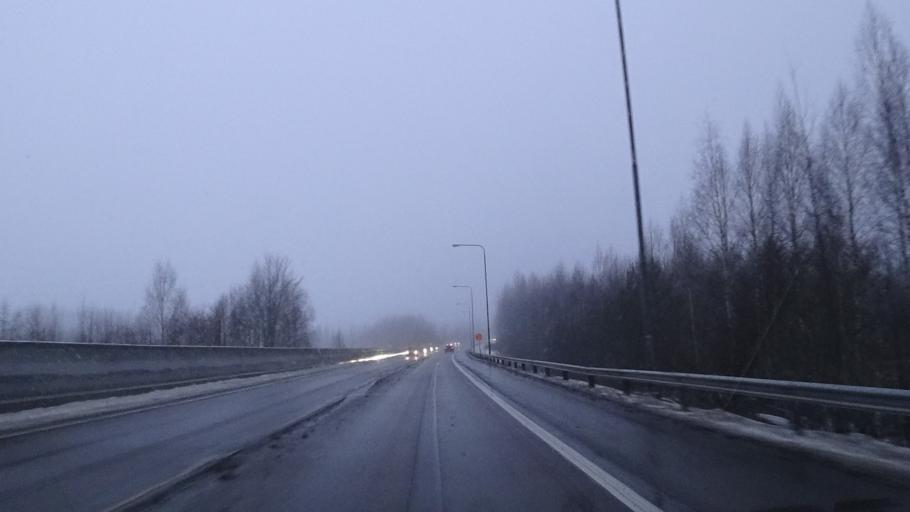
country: FI
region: Paijanne Tavastia
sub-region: Lahti
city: Hollola
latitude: 60.9814
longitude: 25.4716
